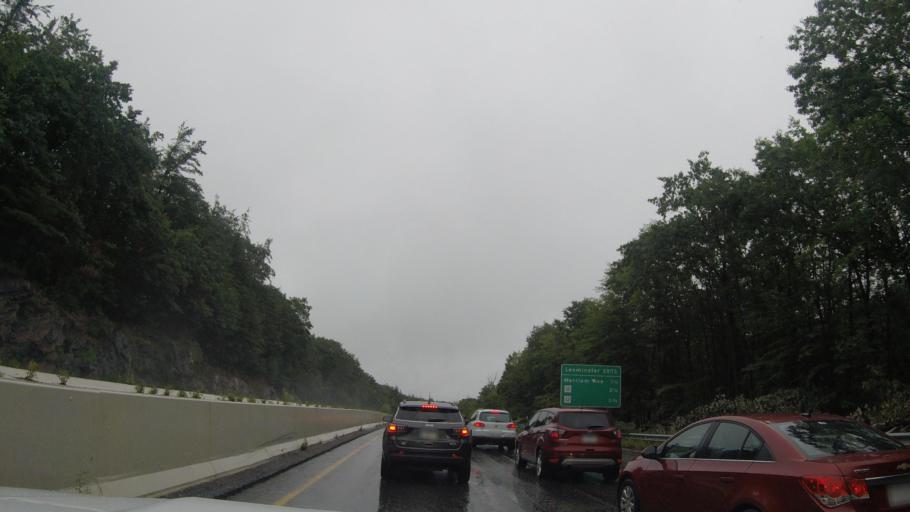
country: US
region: Massachusetts
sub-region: Worcester County
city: Fitchburg
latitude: 42.5502
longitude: -71.8028
